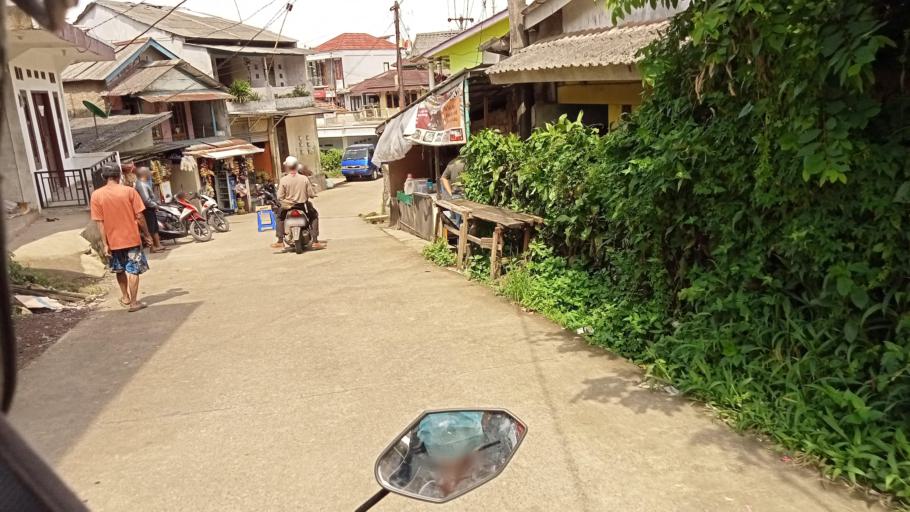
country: ID
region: West Java
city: Caringin
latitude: -6.6451
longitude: 106.9053
